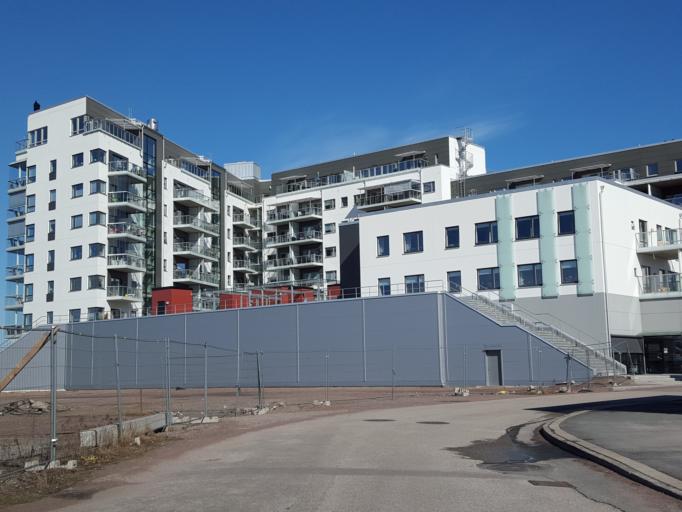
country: SE
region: Kalmar
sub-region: Kalmar Kommun
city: Kalmar
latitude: 56.6697
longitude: 16.3754
